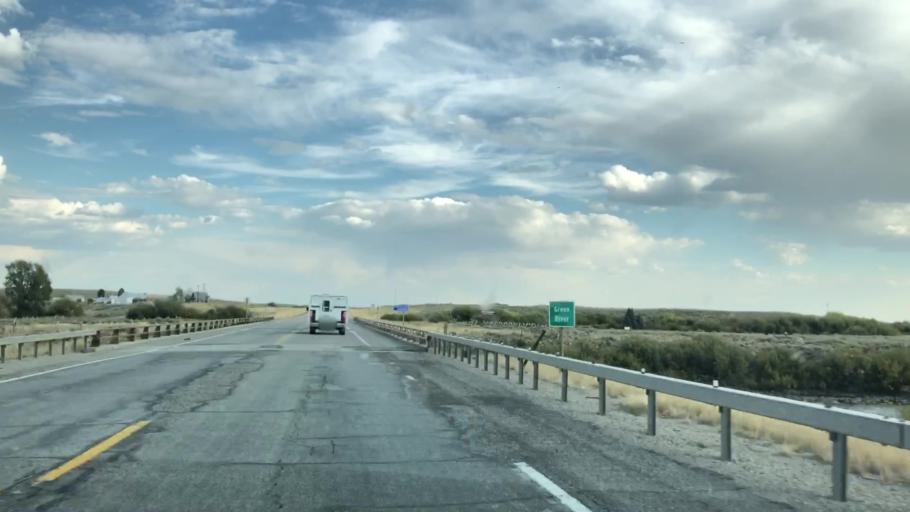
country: US
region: Wyoming
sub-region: Sublette County
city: Pinedale
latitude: 43.0192
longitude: -110.1194
